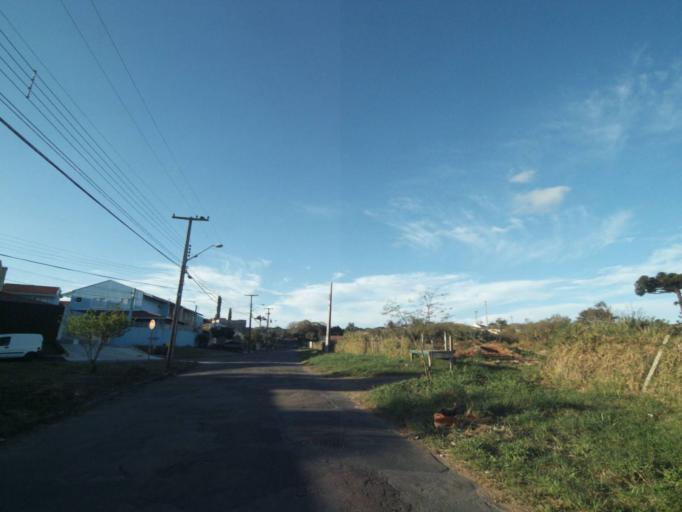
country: BR
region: Parana
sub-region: Curitiba
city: Curitiba
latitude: -25.3784
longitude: -49.2493
